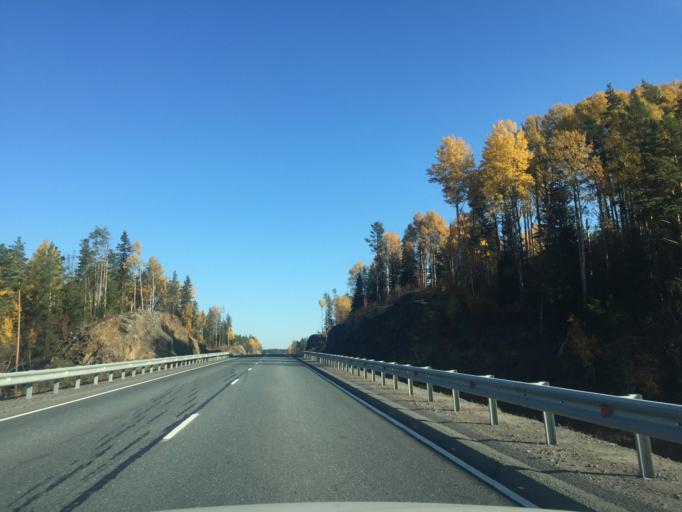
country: RU
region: Leningrad
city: Kuznechnoye
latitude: 61.3183
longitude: 29.7991
